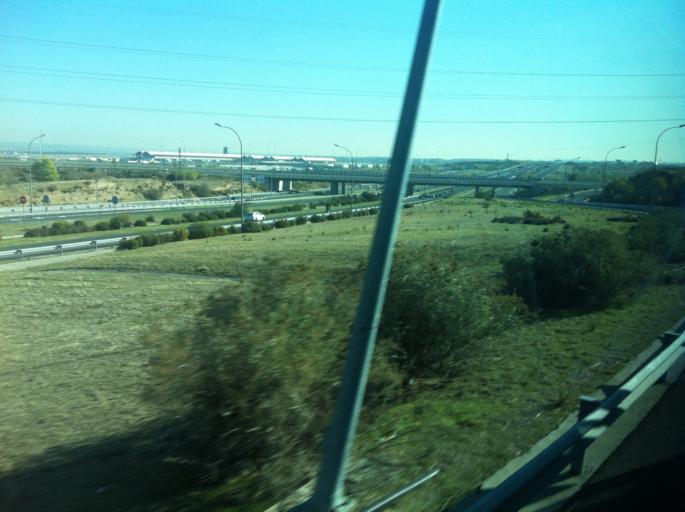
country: ES
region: Madrid
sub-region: Provincia de Madrid
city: San Sebastian de los Reyes
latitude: 40.5086
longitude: -3.6033
